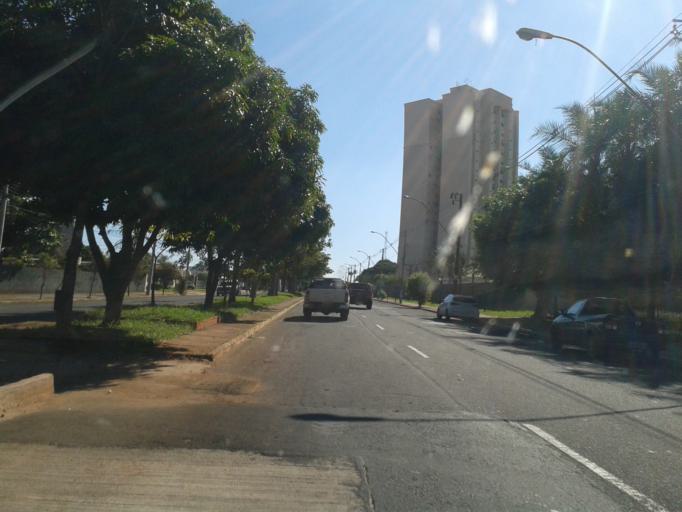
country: BR
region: Minas Gerais
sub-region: Uberaba
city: Uberaba
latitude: -19.7467
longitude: -47.9493
